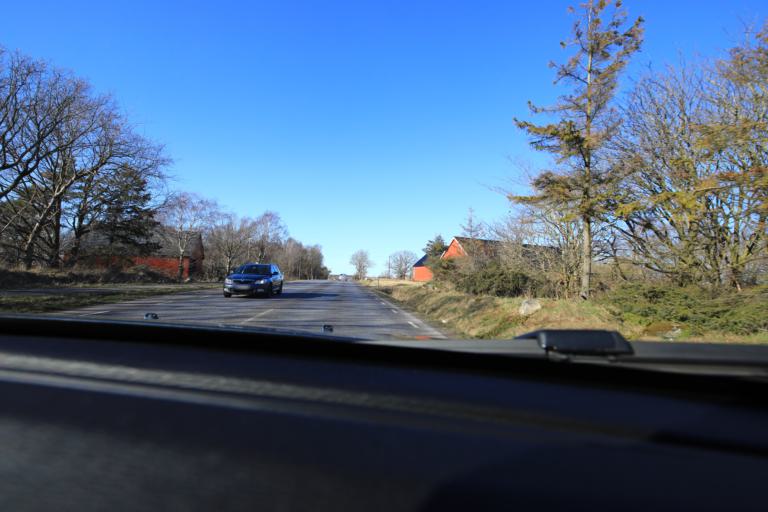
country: SE
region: Halland
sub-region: Varbergs Kommun
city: Traslovslage
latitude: 57.0668
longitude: 12.2922
